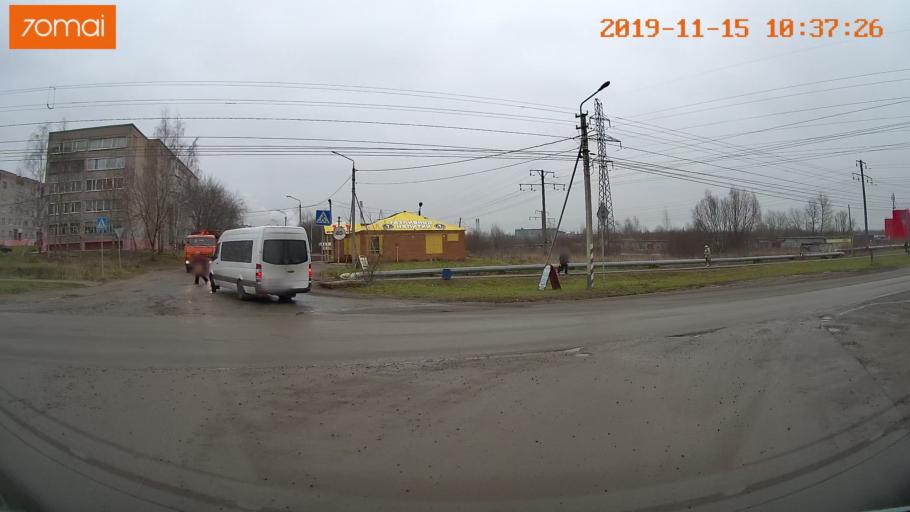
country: RU
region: Vologda
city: Sheksna
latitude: 59.2325
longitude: 38.5126
